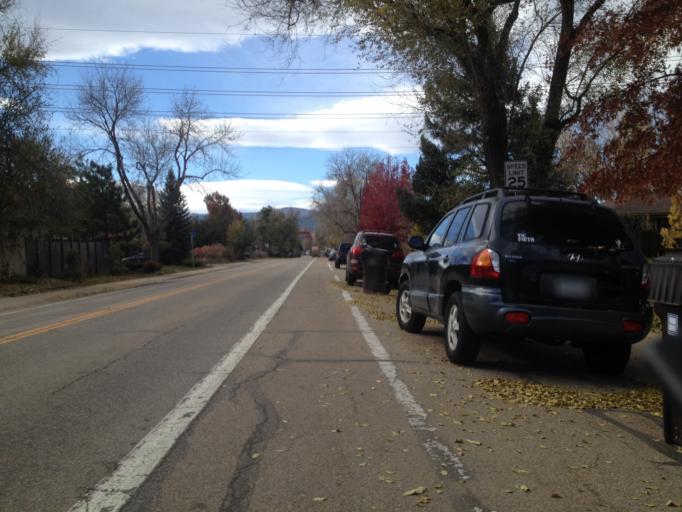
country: US
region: Colorado
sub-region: Boulder County
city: Boulder
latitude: 39.9969
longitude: -105.2542
